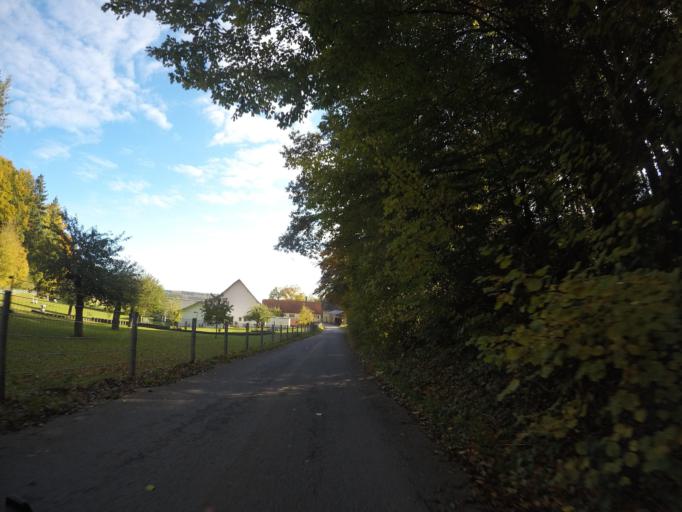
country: DE
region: Baden-Wuerttemberg
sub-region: Tuebingen Region
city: Herbertingen
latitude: 48.0449
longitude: 9.4648
